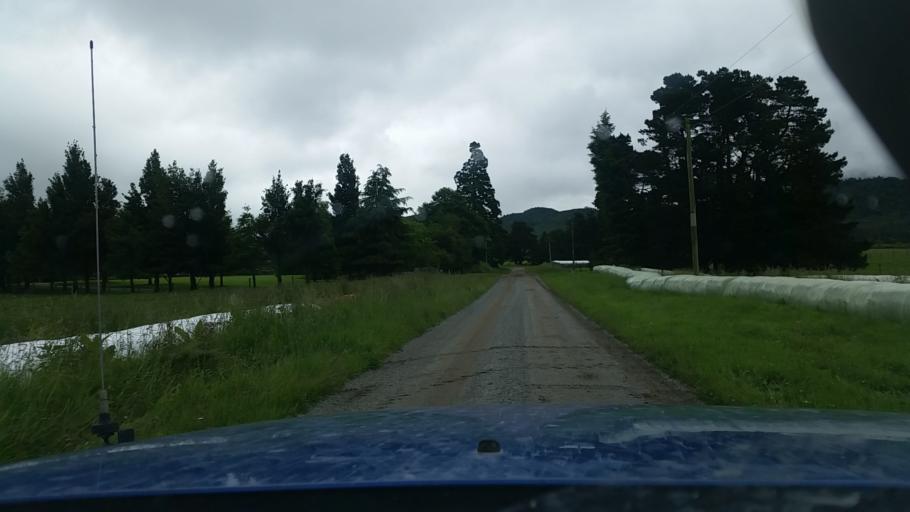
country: NZ
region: Canterbury
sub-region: Ashburton District
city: Methven
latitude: -43.6649
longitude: 171.4167
